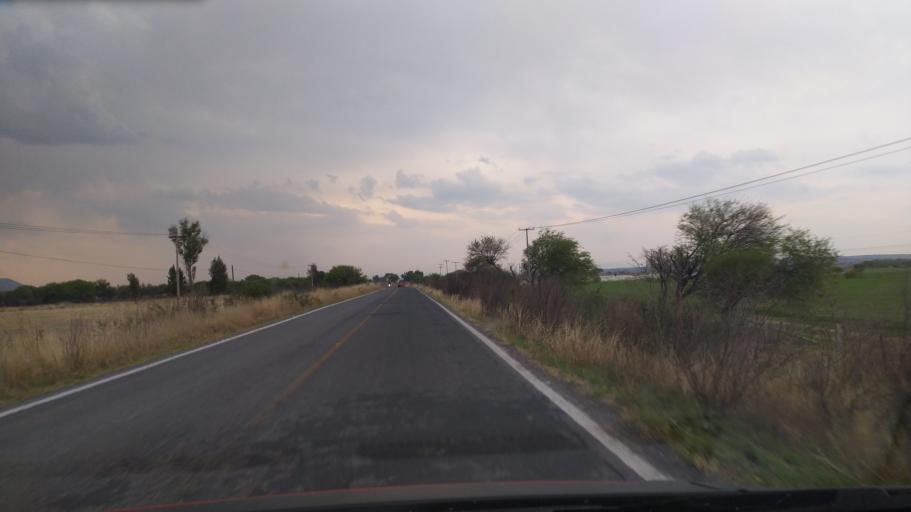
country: MX
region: Guanajuato
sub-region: San Francisco del Rincon
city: San Ignacio de Hidalgo
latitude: 20.8370
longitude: -101.8985
